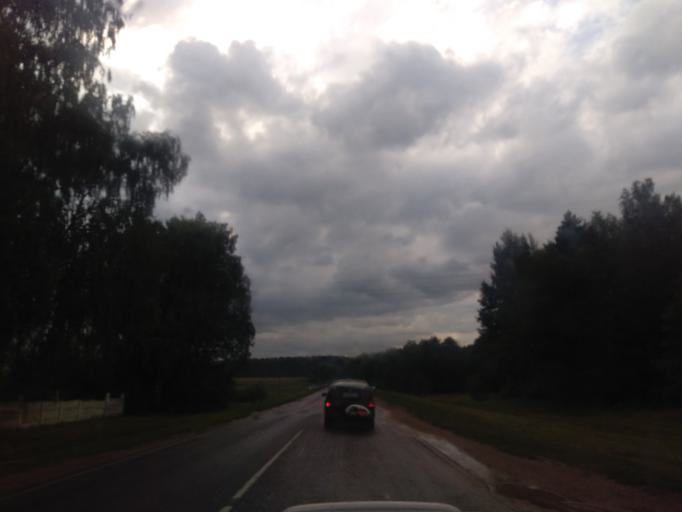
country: BY
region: Minsk
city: Enyerhyetykaw
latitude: 53.5392
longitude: 27.0628
